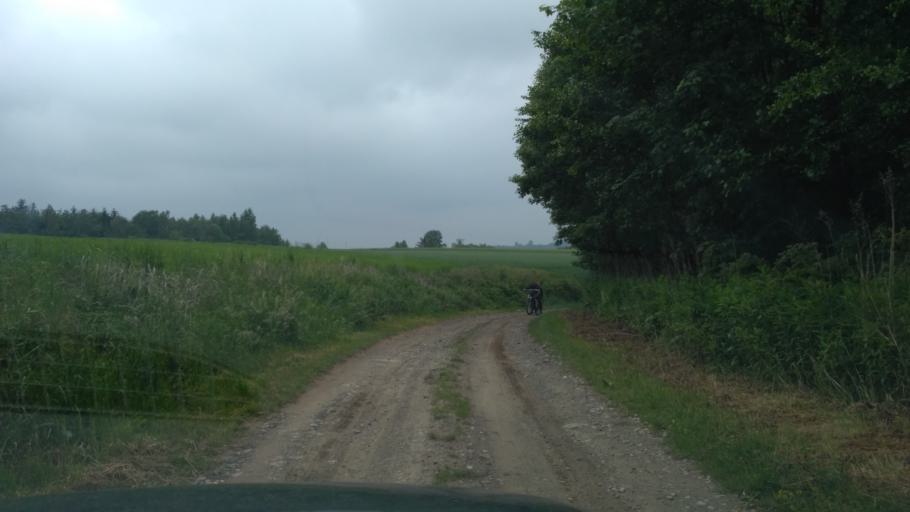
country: PL
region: Subcarpathian Voivodeship
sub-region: Powiat ropczycko-sedziszowski
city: Zagorzyce
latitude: 49.9843
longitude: 21.7060
